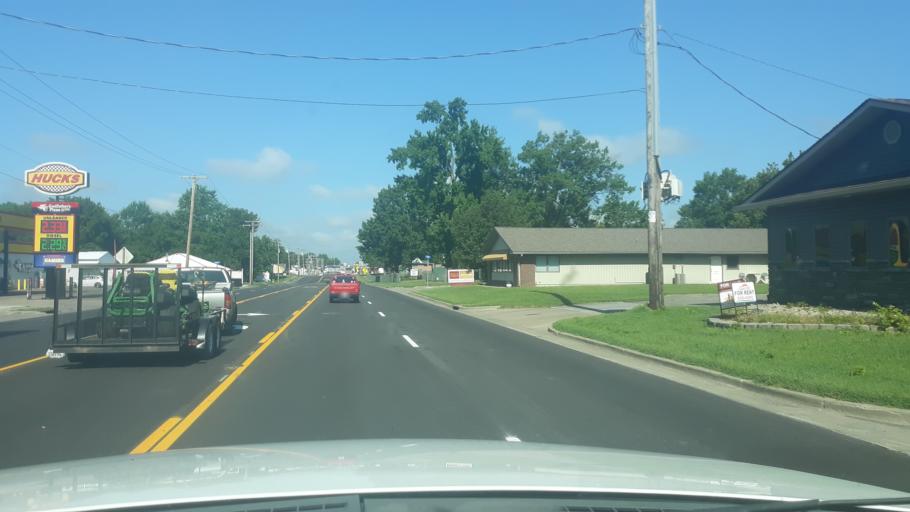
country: US
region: Illinois
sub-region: Williamson County
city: Marion
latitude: 37.7406
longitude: -88.9173
